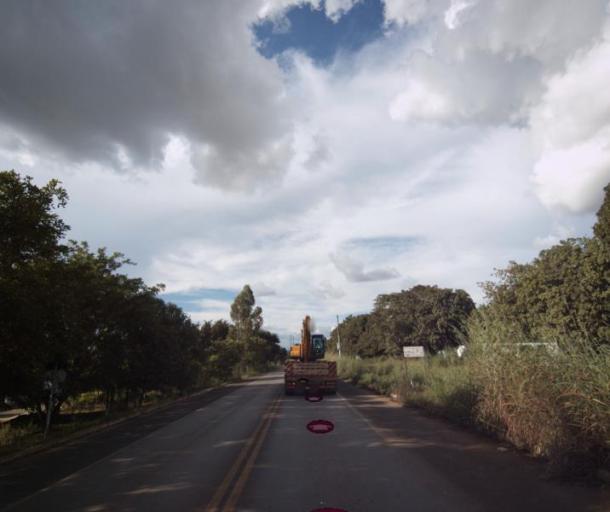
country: BR
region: Goias
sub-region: Niquelandia
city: Niquelandia
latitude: -14.7713
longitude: -48.6254
